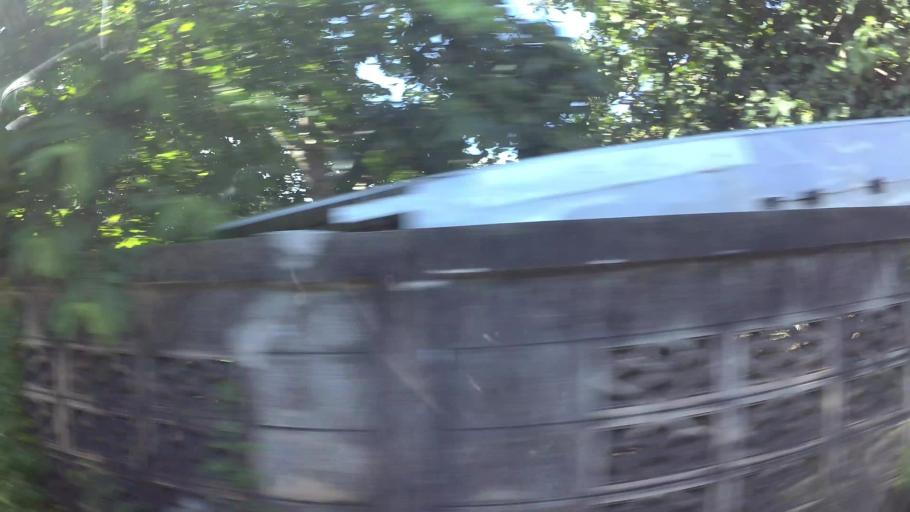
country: TH
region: Rayong
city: Rayong
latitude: 12.6709
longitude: 101.3006
